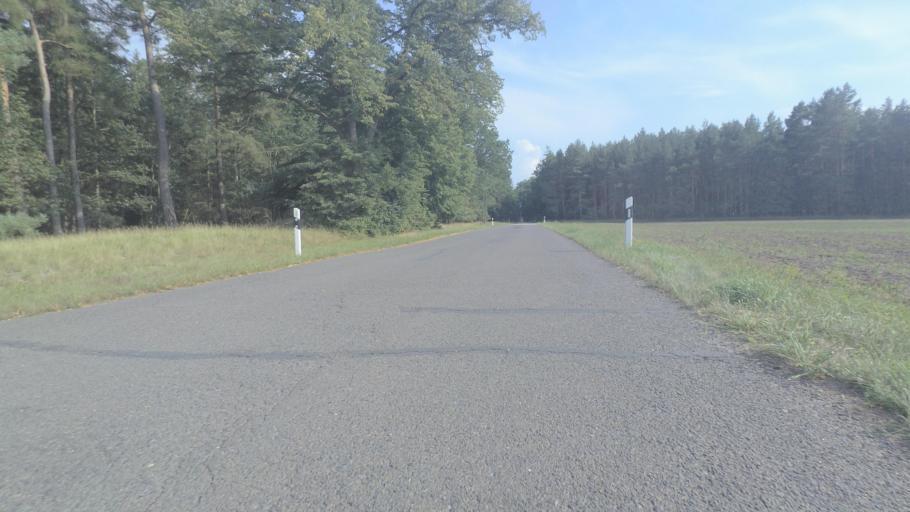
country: DE
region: Brandenburg
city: Wittstock
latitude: 53.2675
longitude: 12.4568
